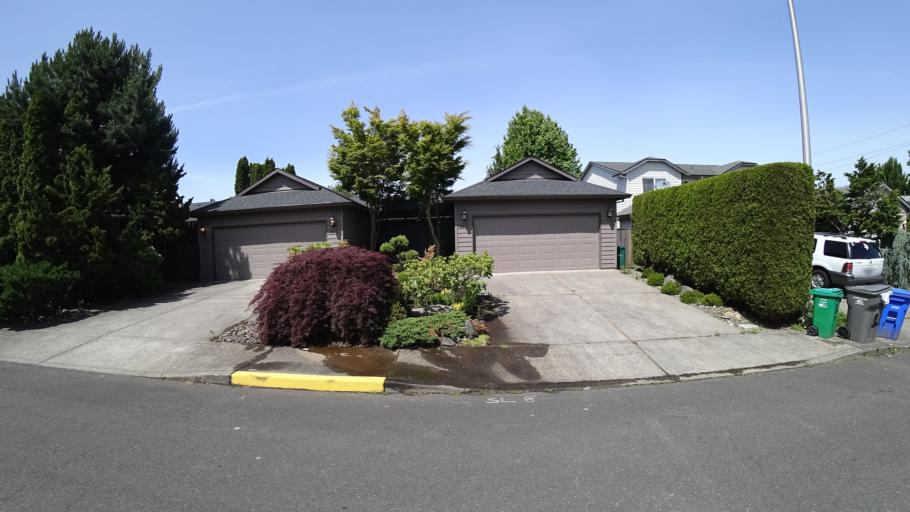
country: US
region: Oregon
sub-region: Multnomah County
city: Fairview
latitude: 45.5514
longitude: -122.5083
